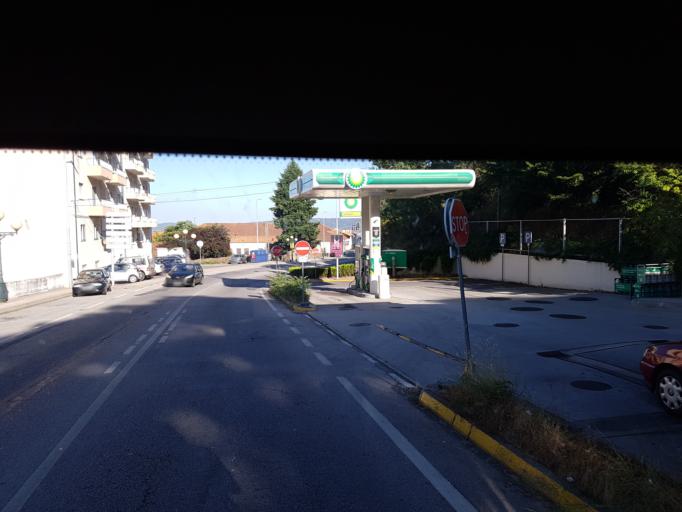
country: PT
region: Castelo Branco
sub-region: Covilha
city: Covilha
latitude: 40.2760
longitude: -7.5058
